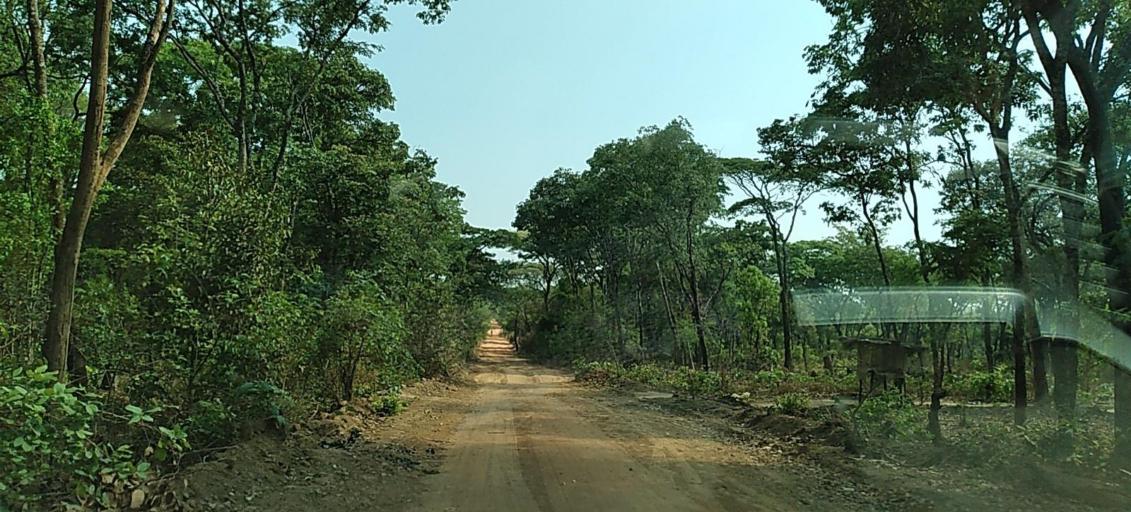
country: ZM
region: Copperbelt
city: Kalulushi
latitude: -12.9183
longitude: 27.8226
